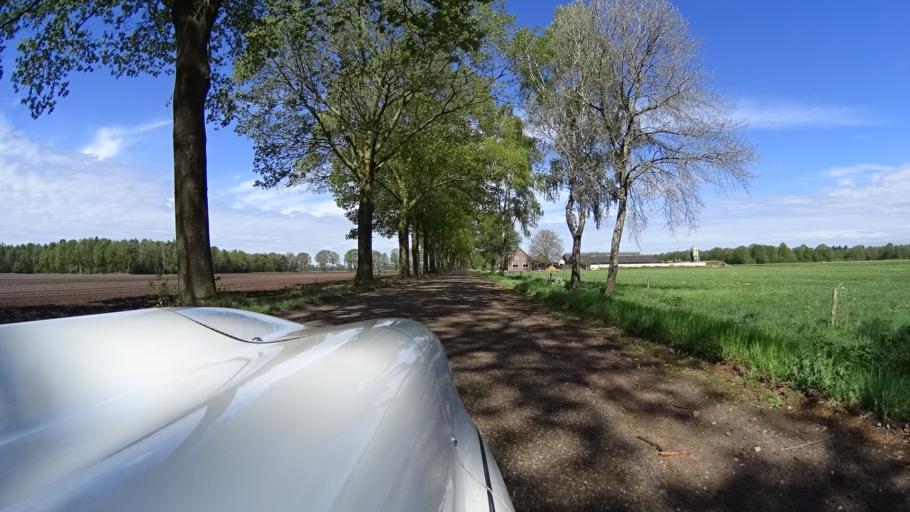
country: NL
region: North Brabant
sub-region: Gemeente Mill en Sint Hubert
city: Wilbertoord
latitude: 51.5983
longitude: 5.8080
